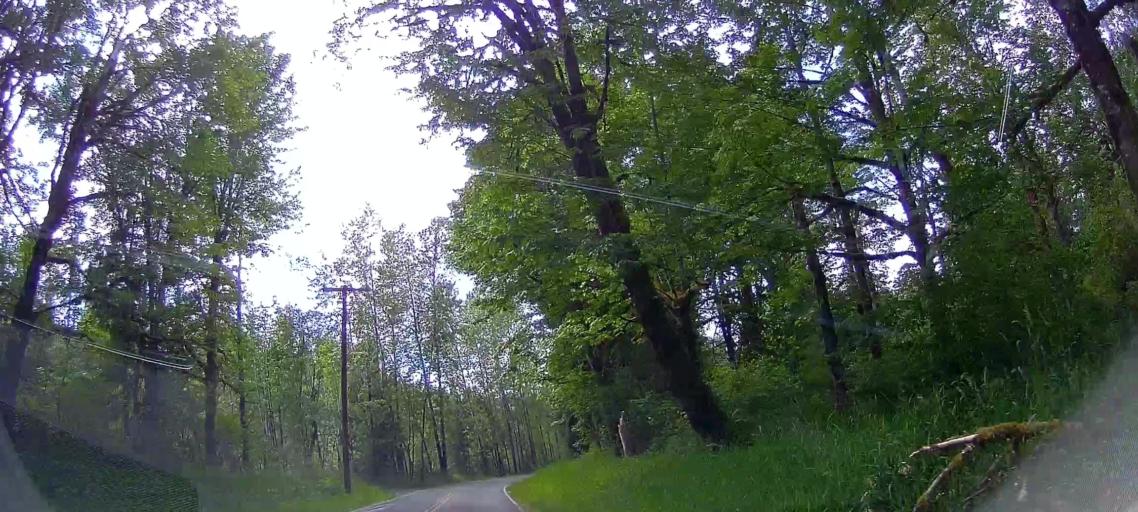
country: US
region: Washington
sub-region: Skagit County
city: Sedro-Woolley
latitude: 48.6757
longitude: -122.1564
